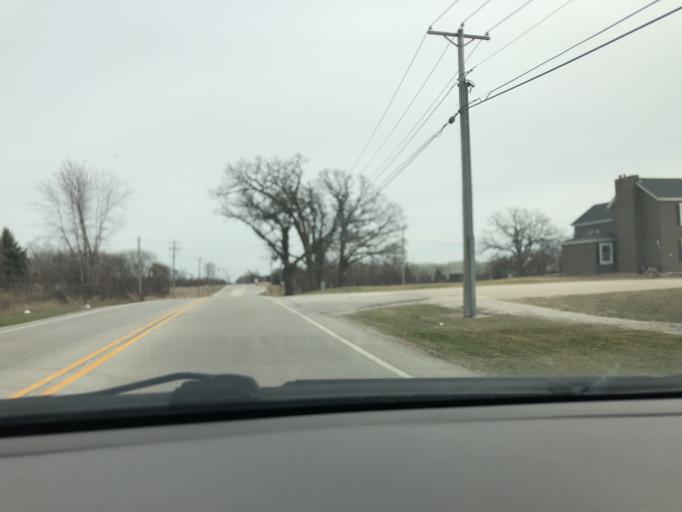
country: US
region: Illinois
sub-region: Kane County
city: Gilberts
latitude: 42.0699
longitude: -88.3459
